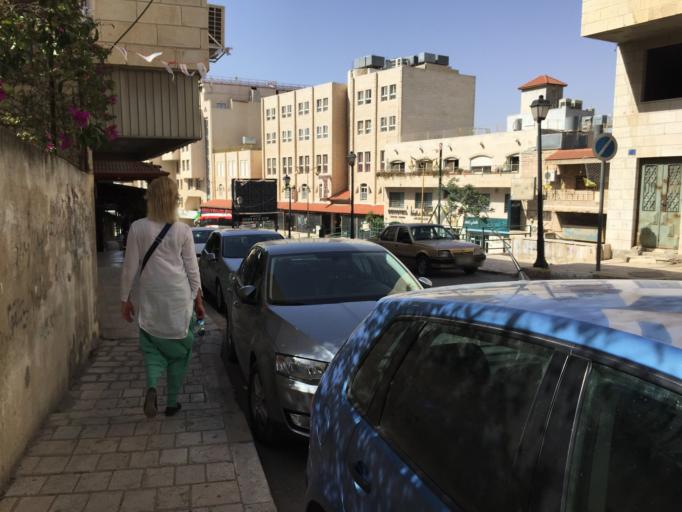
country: PS
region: West Bank
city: Bethlehem
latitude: 31.7108
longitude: 35.2033
